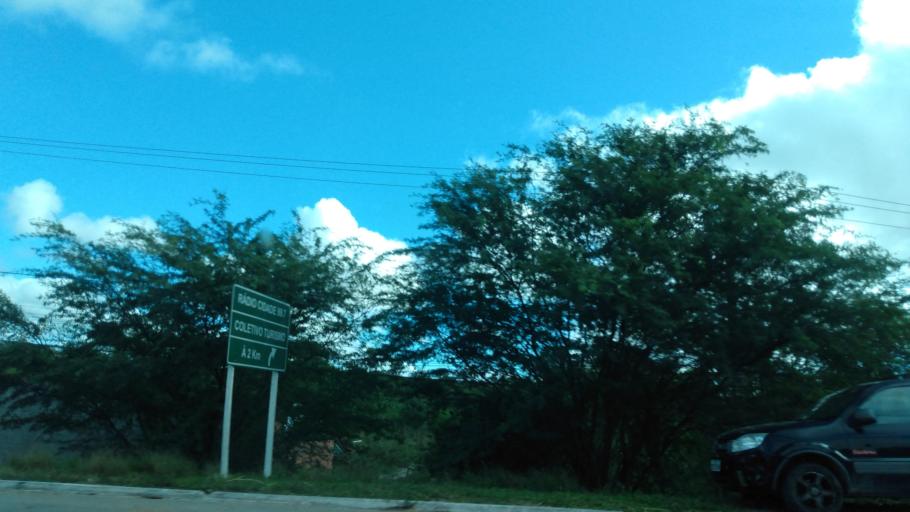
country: BR
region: Pernambuco
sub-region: Caruaru
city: Caruaru
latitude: -8.3008
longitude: -35.9969
